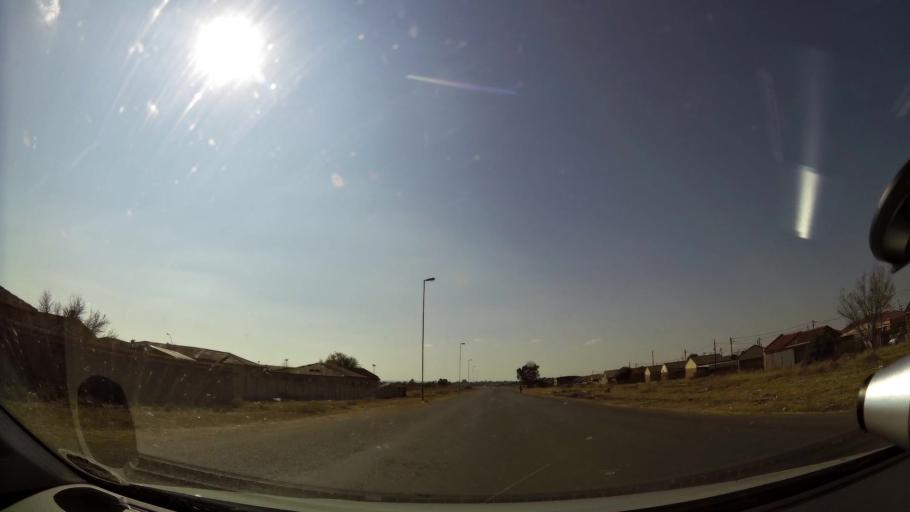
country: ZA
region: Orange Free State
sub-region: Mangaung Metropolitan Municipality
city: Bloemfontein
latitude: -29.1531
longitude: 26.2591
